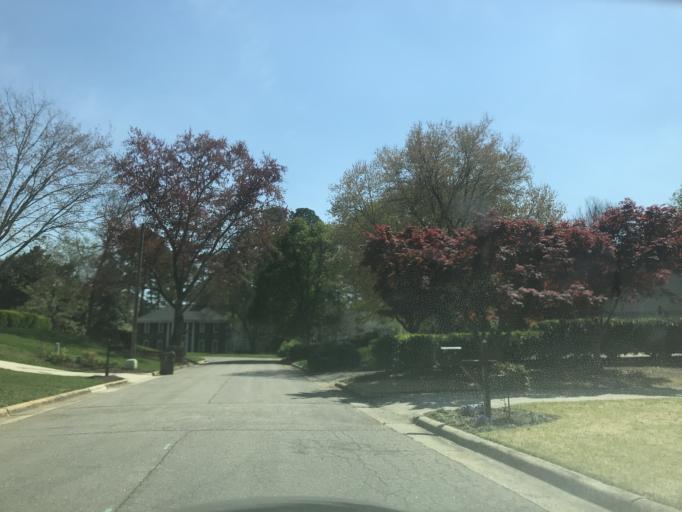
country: US
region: North Carolina
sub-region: Wake County
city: West Raleigh
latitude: 35.8311
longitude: -78.6427
